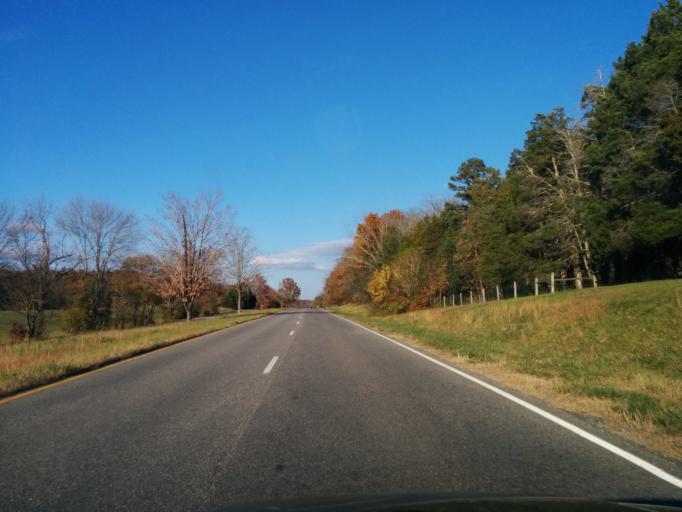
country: US
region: Virginia
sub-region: Rockbridge County
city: East Lexington
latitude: 37.8184
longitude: -79.3926
